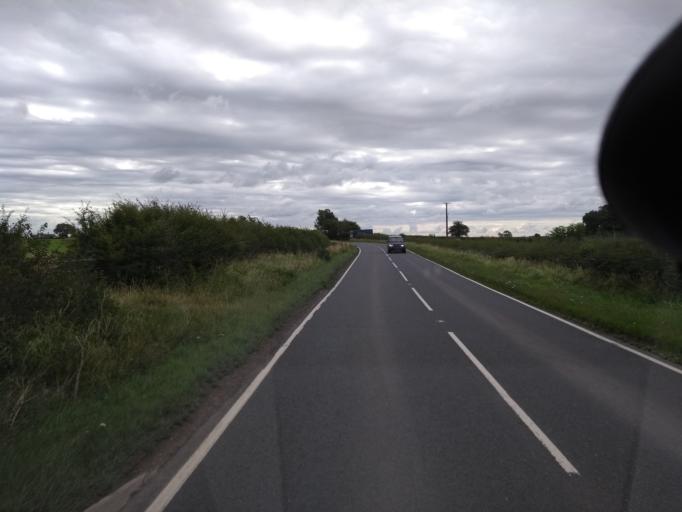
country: GB
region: England
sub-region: Somerset
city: Bridgwater
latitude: 51.1764
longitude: -3.0866
